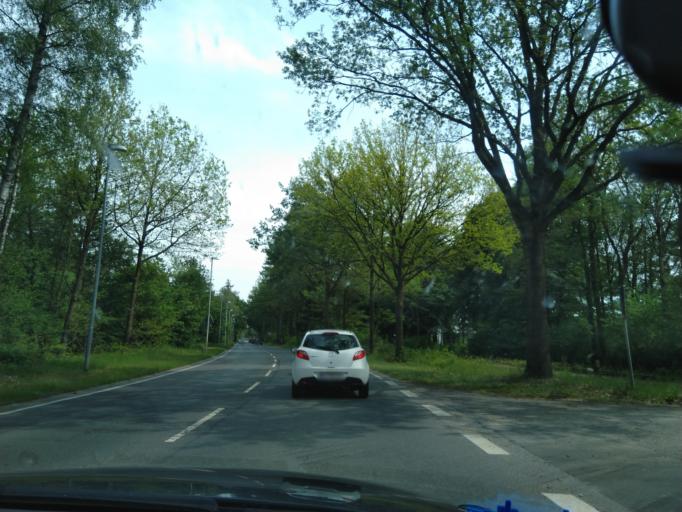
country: DE
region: Lower Saxony
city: Nordhorn
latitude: 52.4164
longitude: 7.0363
